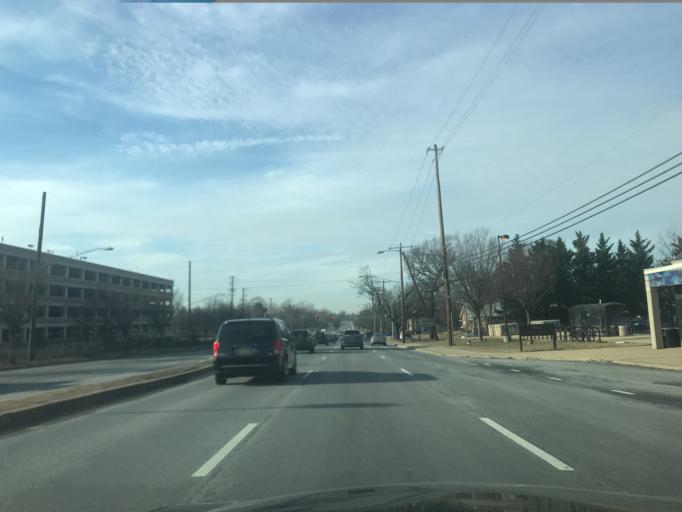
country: US
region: Maryland
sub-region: Montgomery County
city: Glenmont
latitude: 39.0619
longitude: -77.0531
